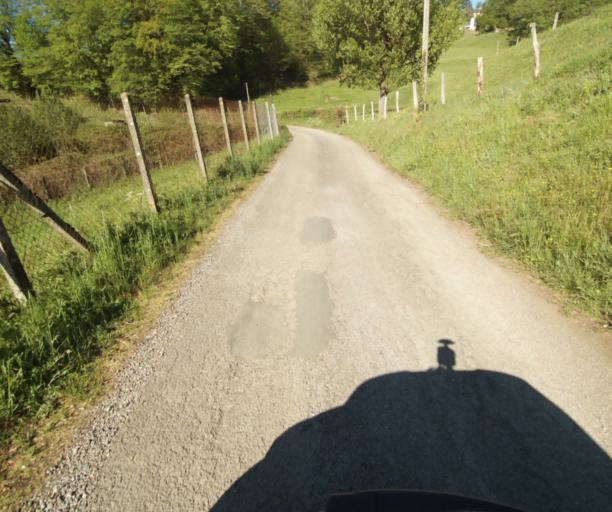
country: FR
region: Limousin
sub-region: Departement de la Correze
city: Tulle
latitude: 45.2801
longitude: 1.7806
